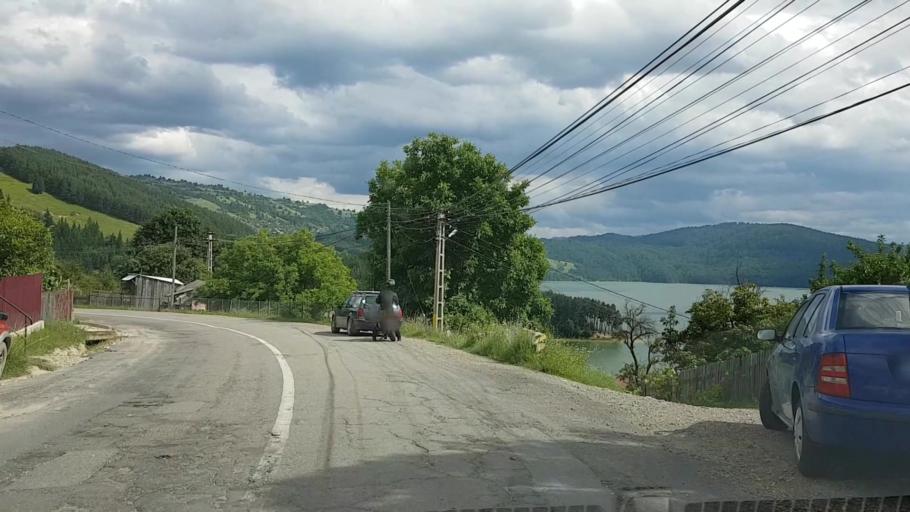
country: RO
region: Neamt
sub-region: Comuna Hangu
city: Hangu
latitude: 47.0181
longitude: 26.0732
